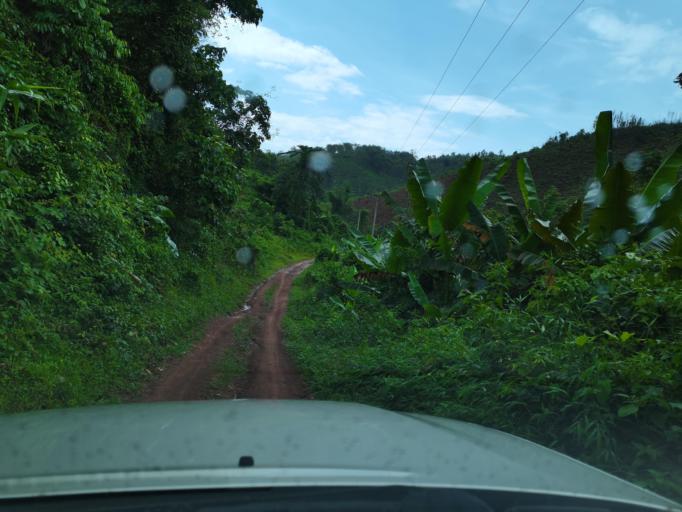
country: LA
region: Loungnamtha
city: Muang Nale
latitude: 20.5237
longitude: 101.0683
